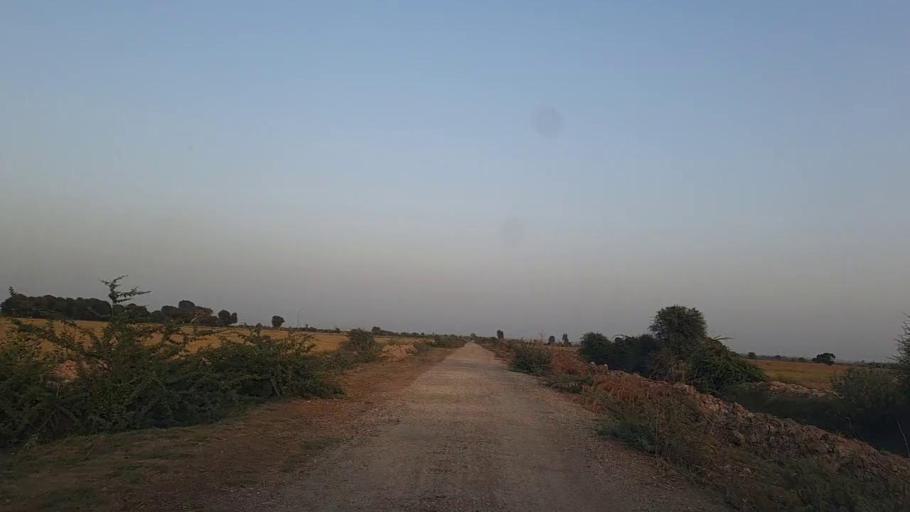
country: PK
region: Sindh
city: Naukot
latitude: 24.6955
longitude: 69.2761
